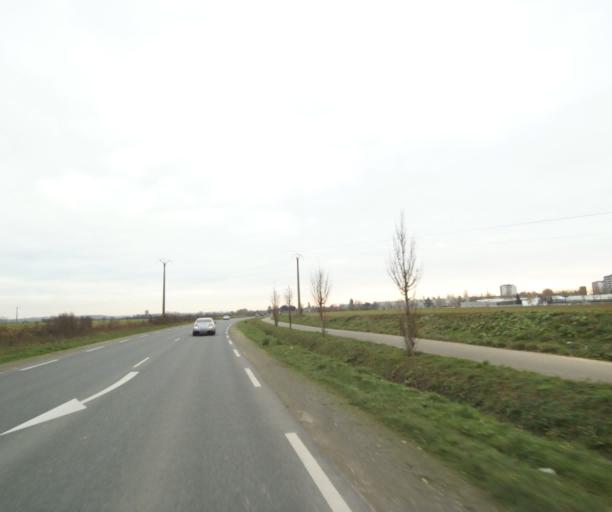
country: FR
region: Ile-de-France
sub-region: Departement du Val-d'Oise
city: Arnouville
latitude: 49.0081
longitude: 2.4250
